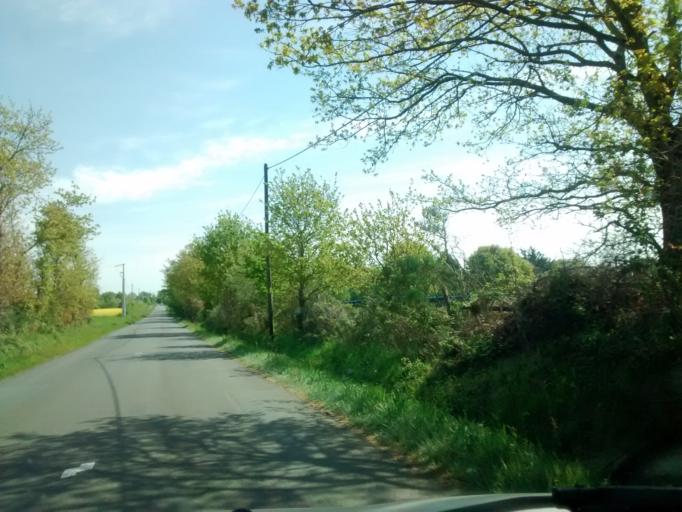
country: FR
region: Brittany
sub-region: Departement d'Ille-et-Vilaine
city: Messac
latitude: 47.8038
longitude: -1.7602
